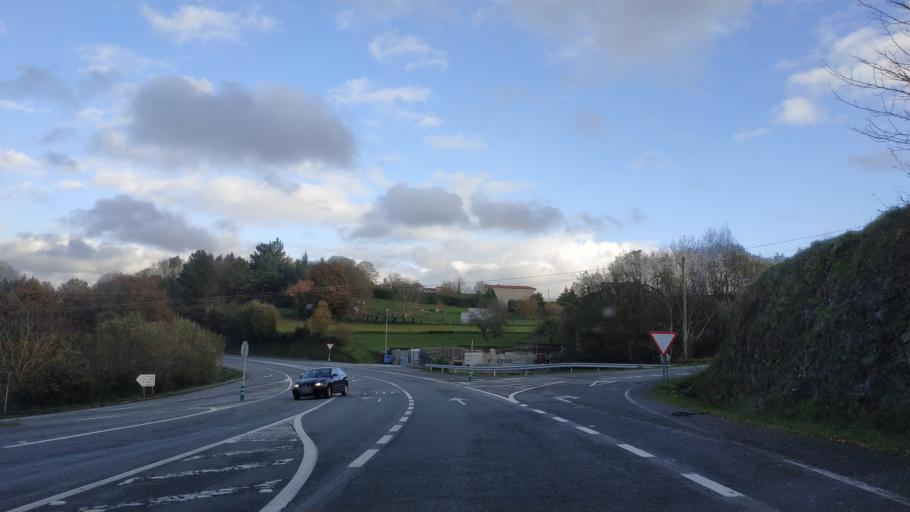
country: ES
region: Galicia
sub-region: Provincia de Pontevedra
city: Silleda
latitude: 42.7952
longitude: -8.1697
